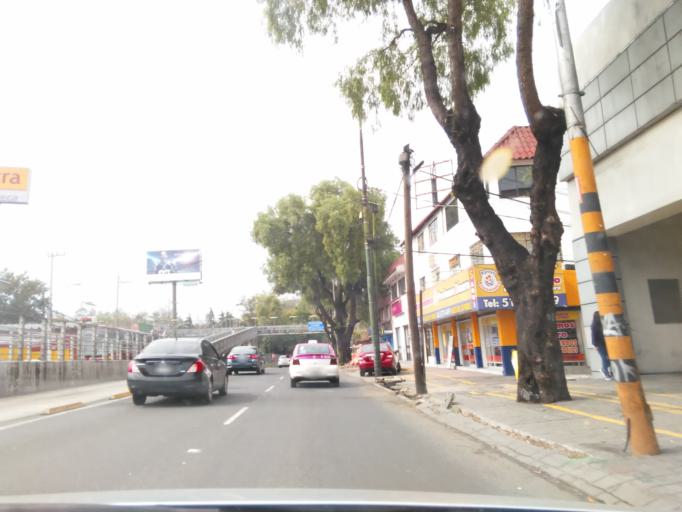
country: MX
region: Mexico City
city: Tlalpan
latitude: 19.2943
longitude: -99.1813
